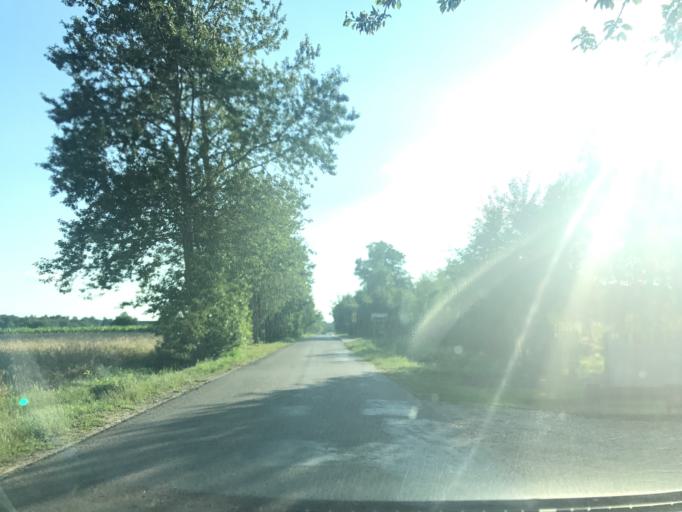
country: PL
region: Greater Poland Voivodeship
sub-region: Powiat turecki
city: Wladyslawow
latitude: 52.0986
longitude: 18.3889
